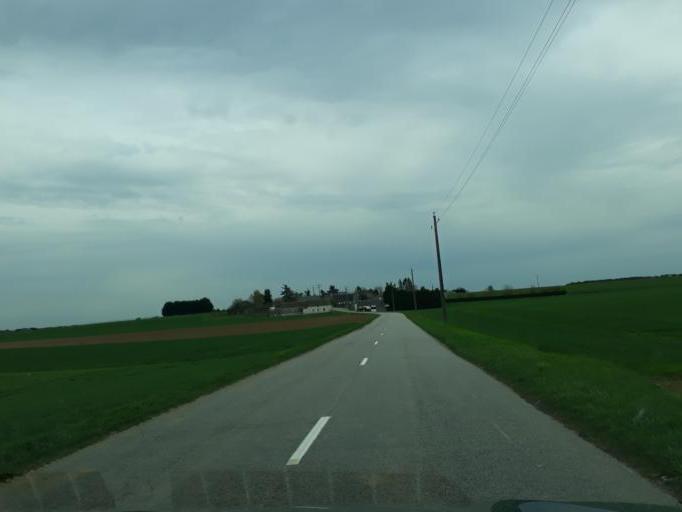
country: FR
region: Centre
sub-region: Departement du Loiret
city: Epieds-en-Beauce
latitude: 47.9219
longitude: 1.5895
